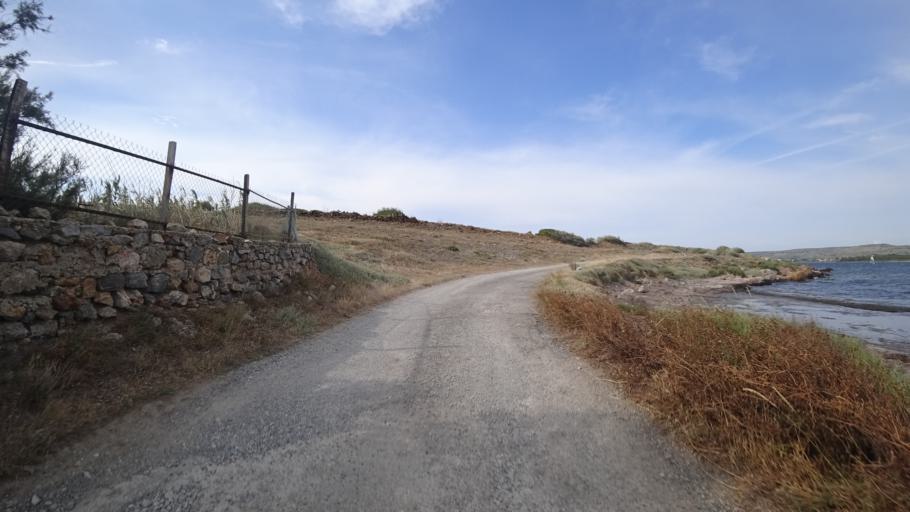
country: FR
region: Languedoc-Roussillon
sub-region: Departement de l'Aude
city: Leucate
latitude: 42.9008
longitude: 3.0186
